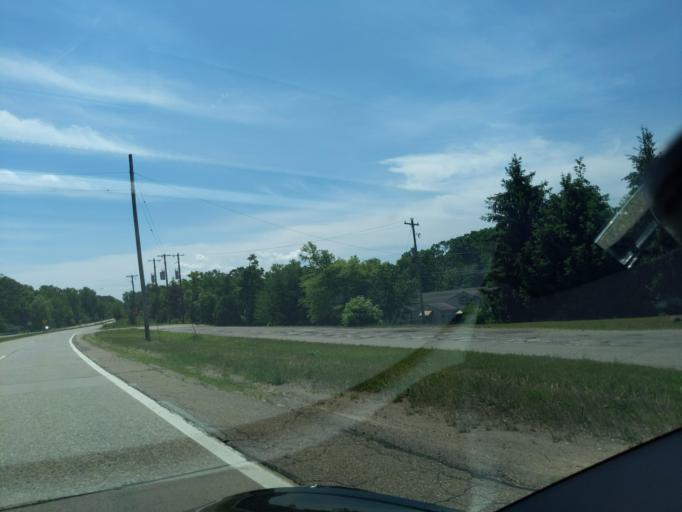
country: US
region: Michigan
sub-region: Kent County
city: Forest Hills
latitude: 42.9531
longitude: -85.4668
